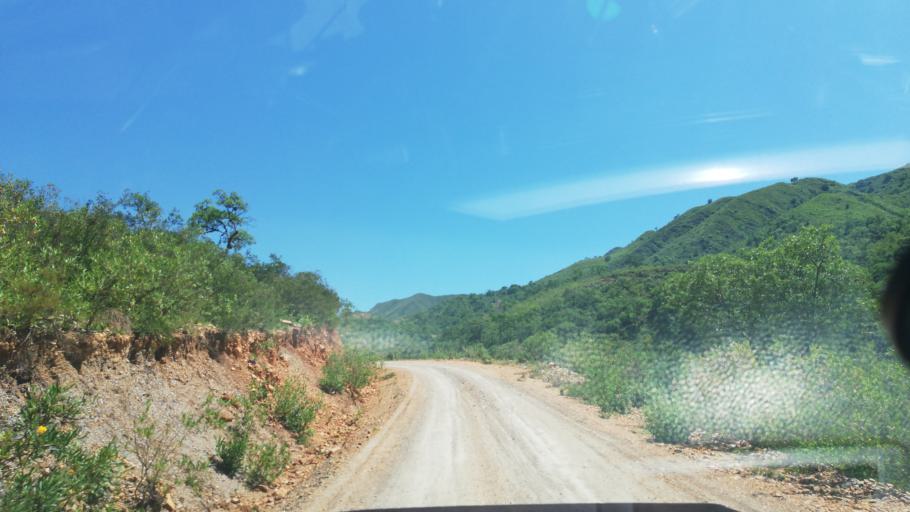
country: BO
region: Cochabamba
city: Mizque
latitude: -17.8785
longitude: -65.2899
